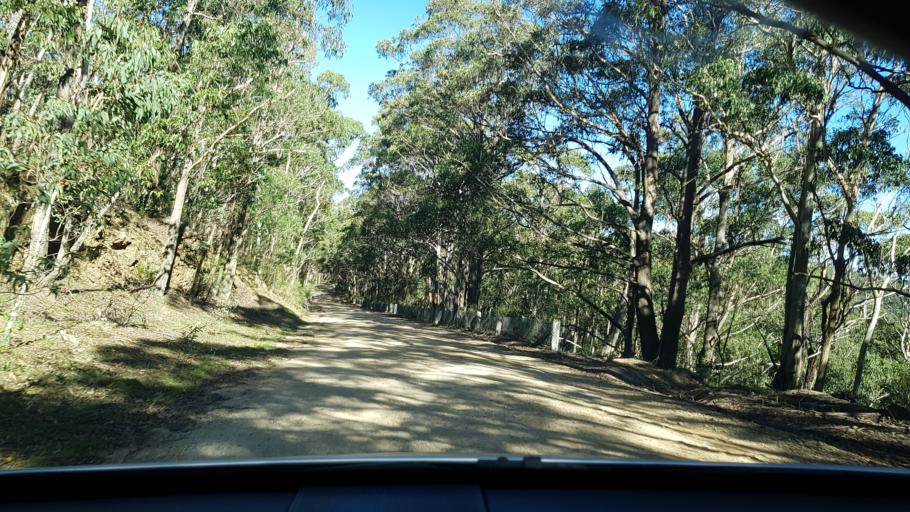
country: AU
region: New South Wales
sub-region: Oberon
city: Oberon
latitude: -33.8573
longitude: 150.0405
